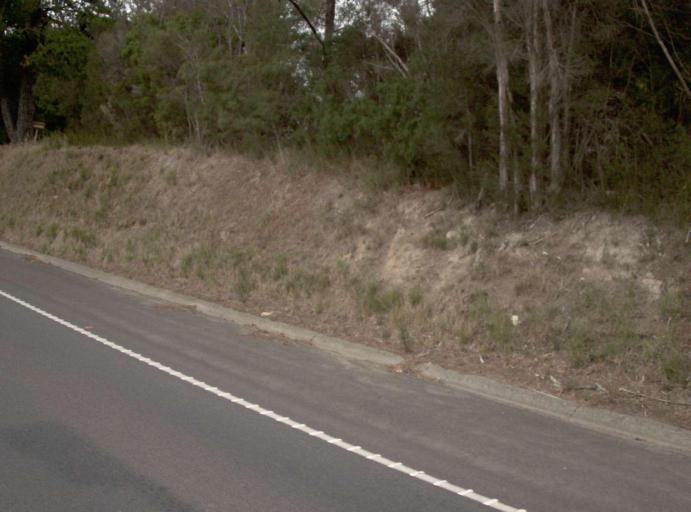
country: AU
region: Victoria
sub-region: Yarra Ranges
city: Yarra Glen
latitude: -37.5938
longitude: 145.4154
